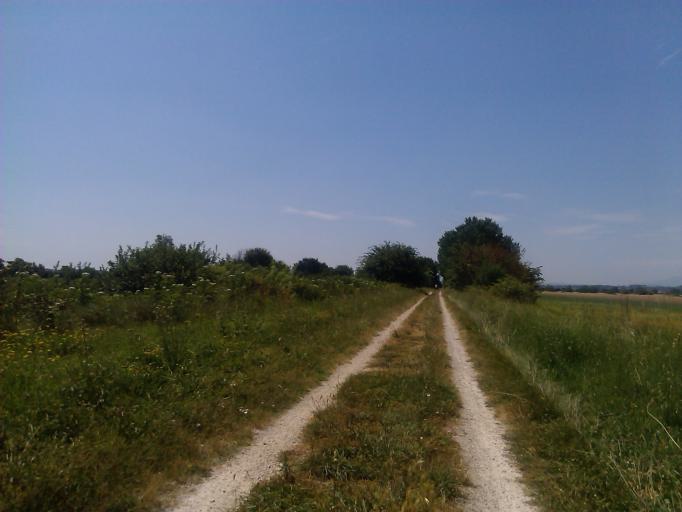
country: IT
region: Tuscany
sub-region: Province of Arezzo
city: Cesa
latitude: 43.3484
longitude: 11.8264
